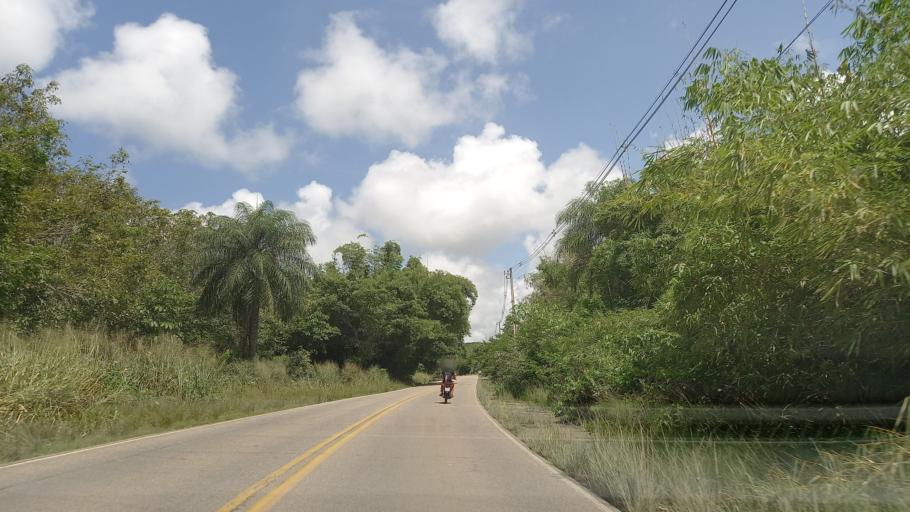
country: BR
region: Pernambuco
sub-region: Sirinhaem
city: Sirinhaem
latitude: -8.6418
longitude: -35.1185
